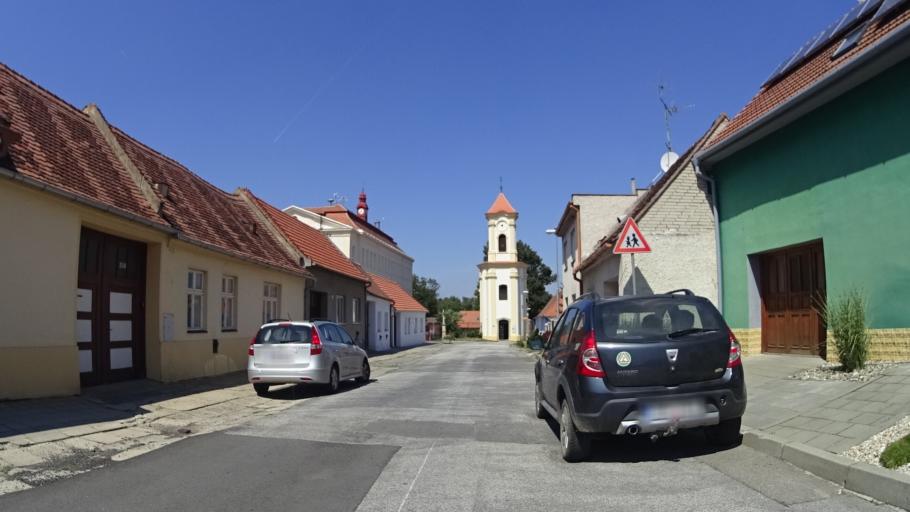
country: CZ
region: South Moravian
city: Straznice
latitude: 48.8977
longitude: 17.3077
